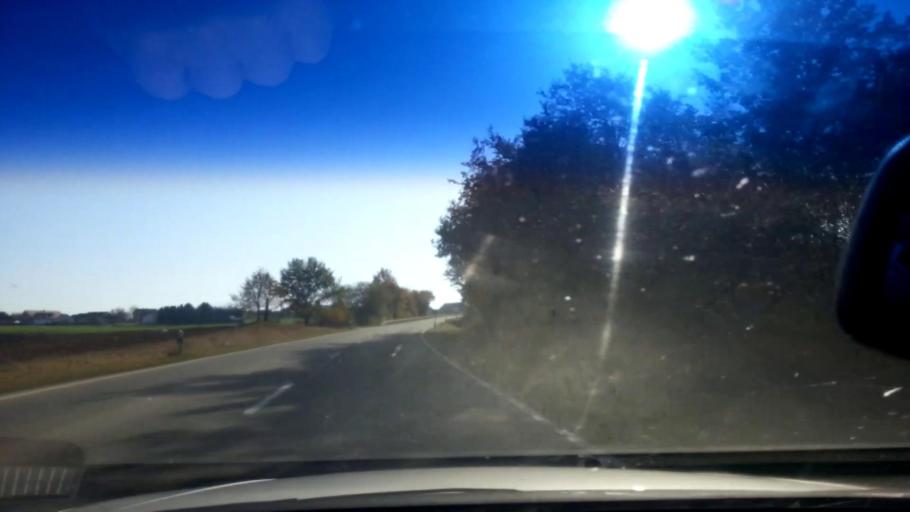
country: DE
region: Bavaria
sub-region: Upper Franconia
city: Stadelhofen
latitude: 49.9912
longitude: 11.2246
